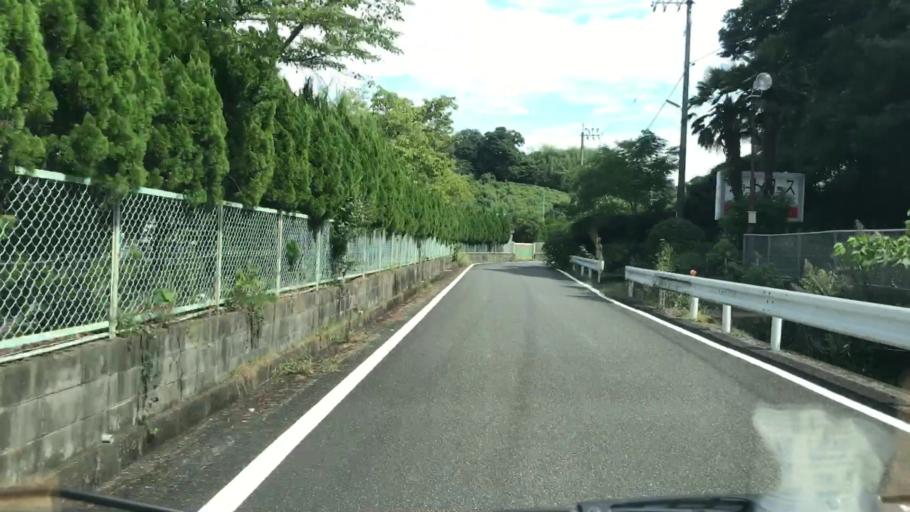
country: JP
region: Saga Prefecture
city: Saga-shi
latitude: 33.2300
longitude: 130.1774
